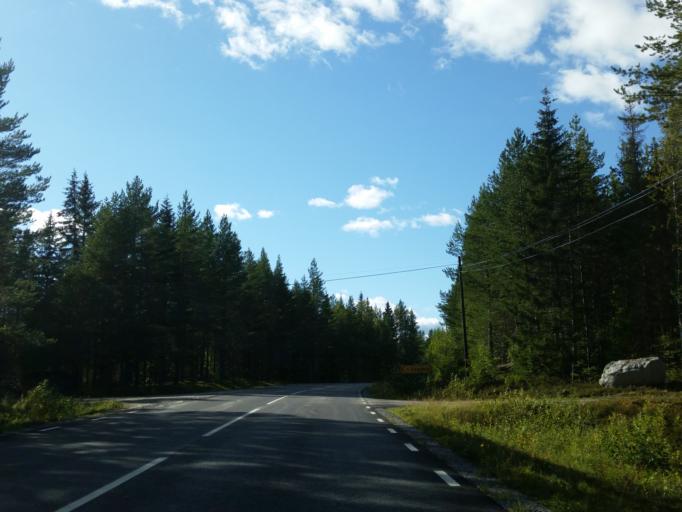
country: SE
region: Vaesterbotten
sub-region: Robertsfors Kommun
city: Robertsfors
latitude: 64.1601
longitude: 20.9437
